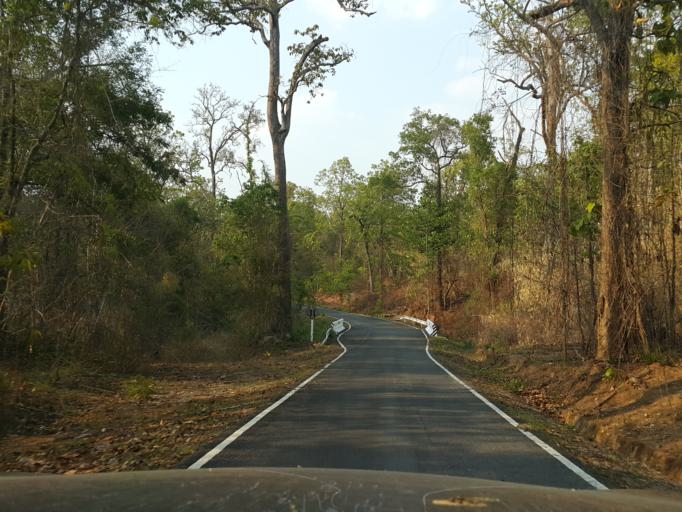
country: TH
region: Lamphun
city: Li
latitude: 17.6301
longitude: 98.8742
